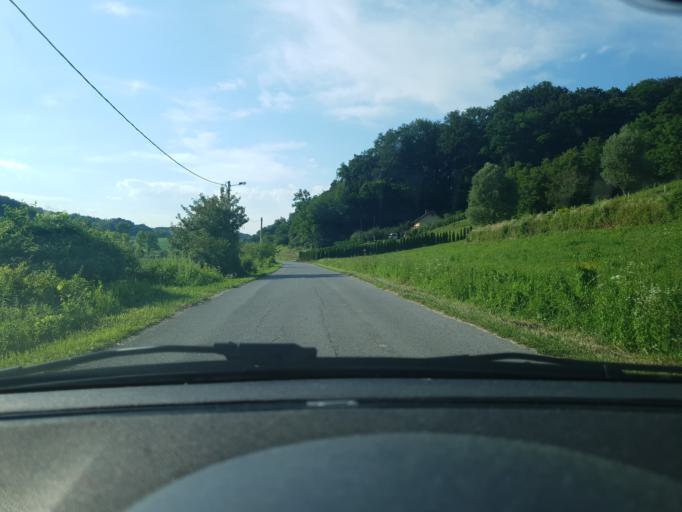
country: HR
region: Krapinsko-Zagorska
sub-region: Grad Krapina
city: Krapina
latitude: 46.1349
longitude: 15.8560
